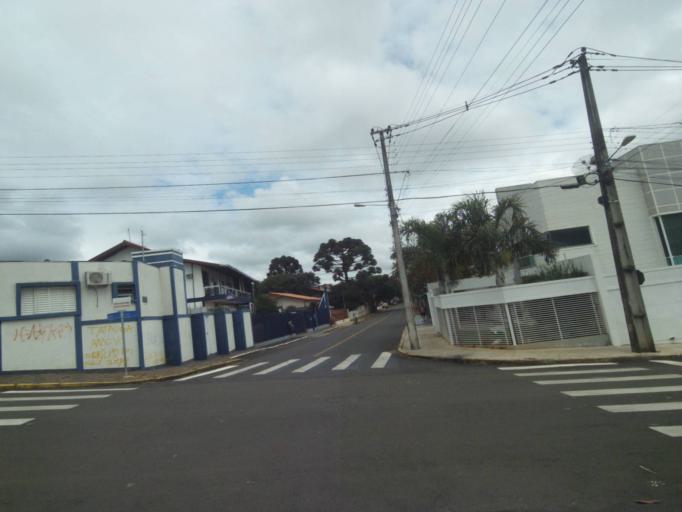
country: BR
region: Parana
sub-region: Telemaco Borba
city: Telemaco Borba
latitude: -24.3361
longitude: -50.6250
